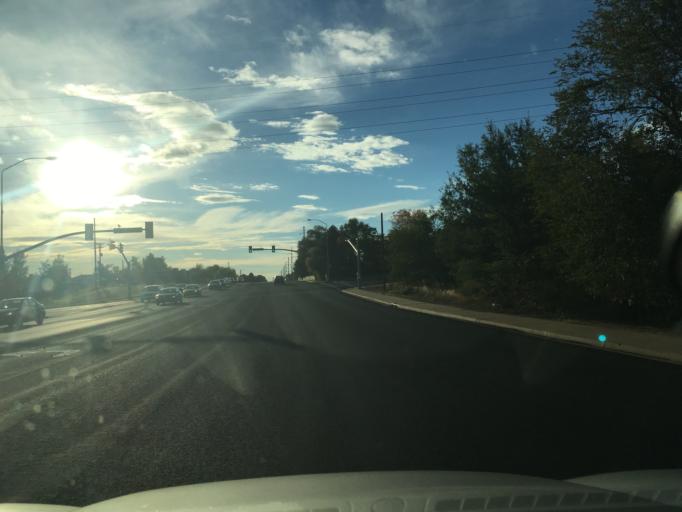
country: US
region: Utah
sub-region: Davis County
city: Layton
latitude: 41.0746
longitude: -111.9575
